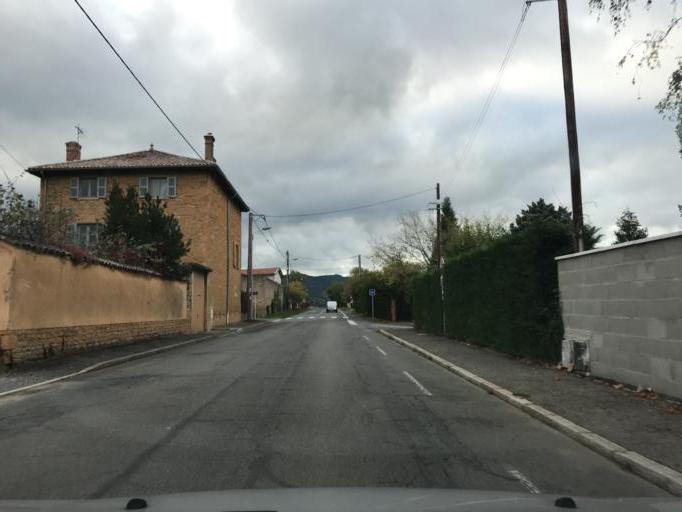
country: FR
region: Rhone-Alpes
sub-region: Departement du Rhone
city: Denice
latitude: 45.9990
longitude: 4.6431
